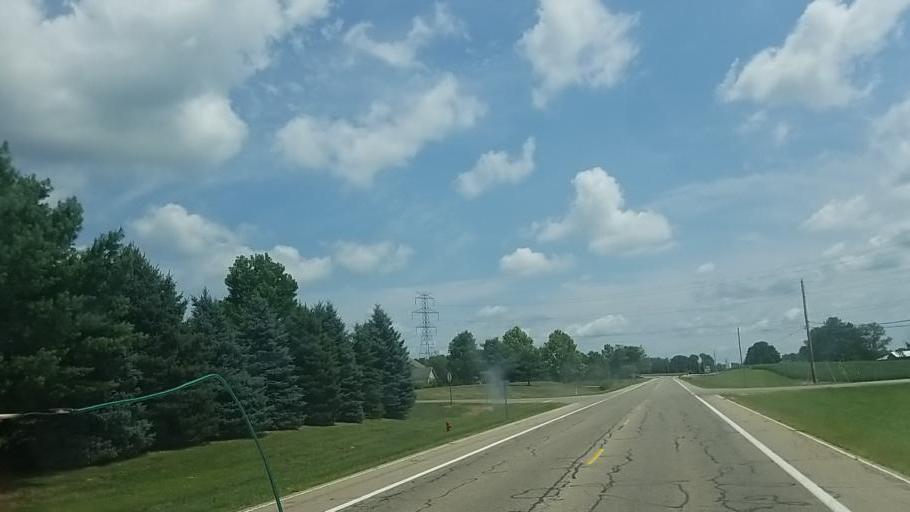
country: US
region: Ohio
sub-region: Fairfield County
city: Pickerington
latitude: 39.8775
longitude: -82.7218
